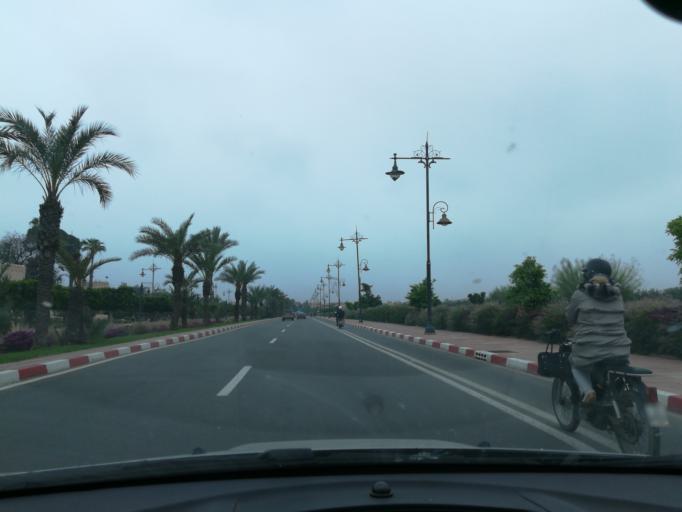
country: MA
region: Marrakech-Tensift-Al Haouz
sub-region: Marrakech
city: Marrakesh
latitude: 31.6181
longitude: -7.9977
